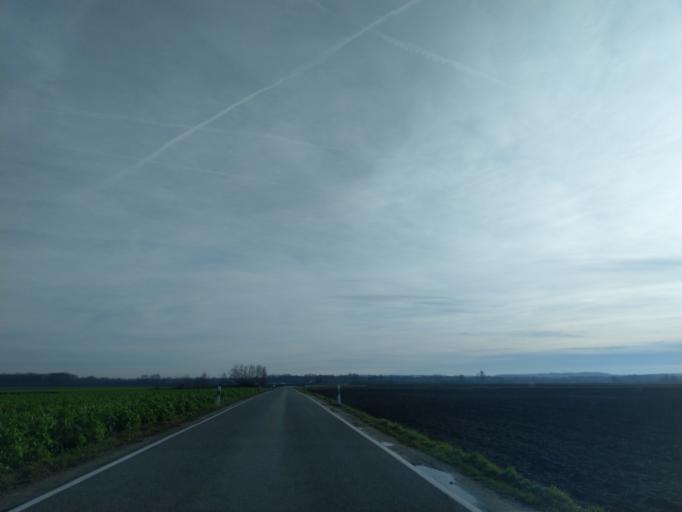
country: DE
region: Bavaria
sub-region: Lower Bavaria
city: Otzing
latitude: 48.7364
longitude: 12.8210
